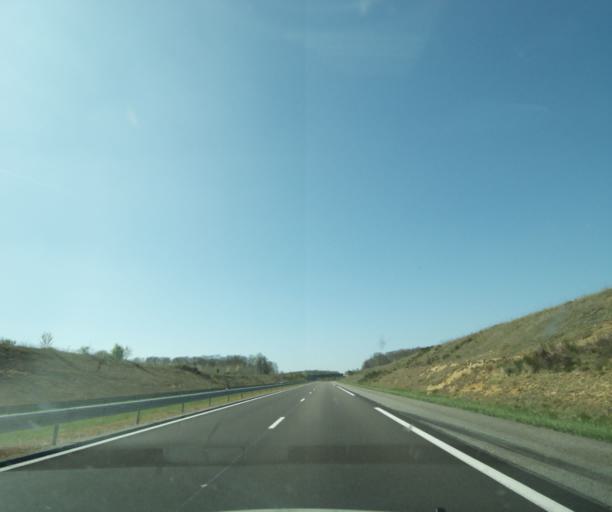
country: FR
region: Centre
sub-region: Departement du Loiret
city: Bonny-sur-Loire
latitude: 47.6101
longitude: 2.8248
